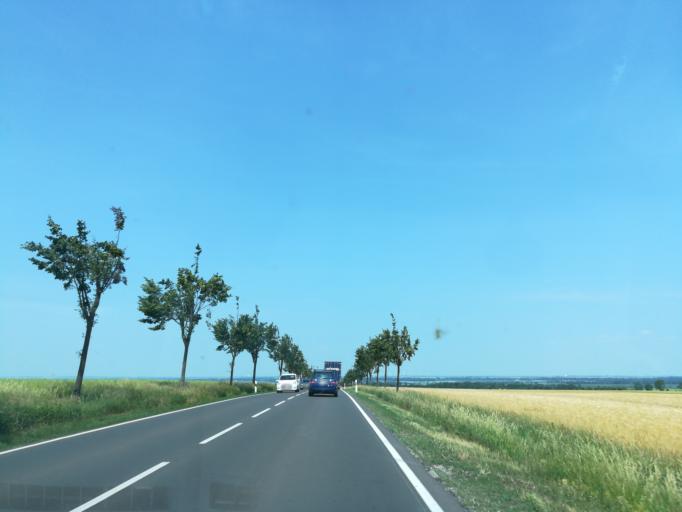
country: DE
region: Saxony-Anhalt
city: Schneidlingen
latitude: 51.8739
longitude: 11.4470
